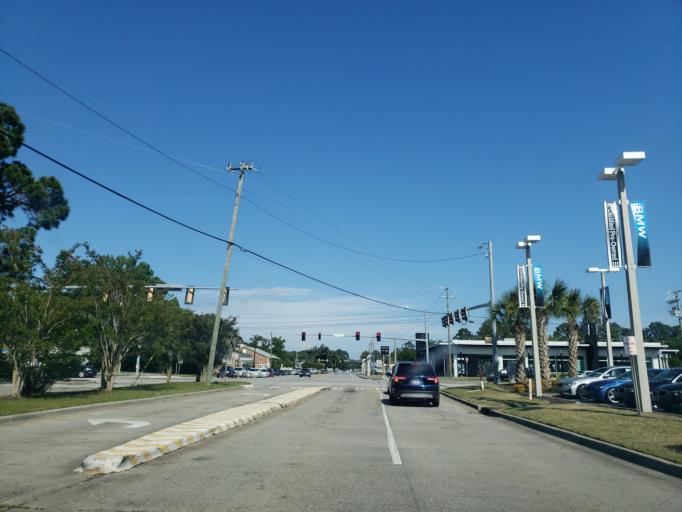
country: US
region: Georgia
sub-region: Chatham County
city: Isle of Hope
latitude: 32.0138
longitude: -81.1139
